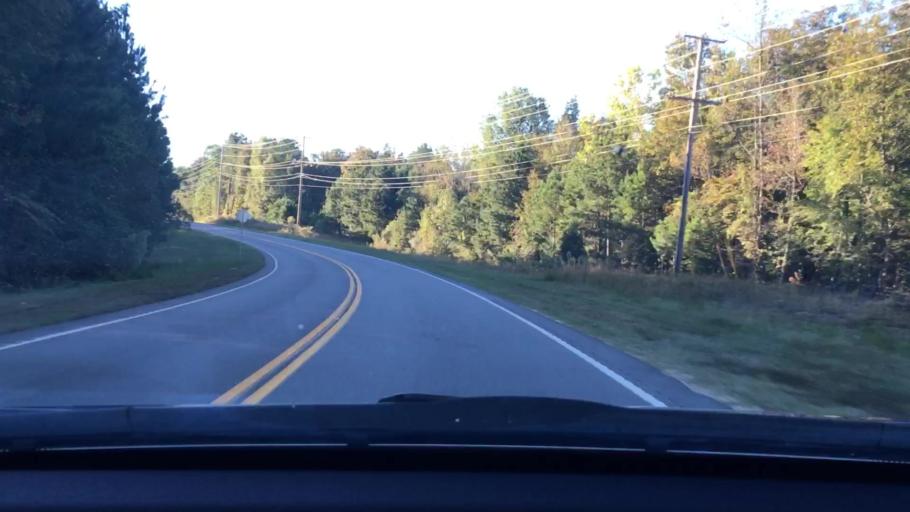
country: US
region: South Carolina
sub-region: Lexington County
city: Irmo
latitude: 34.1013
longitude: -81.1696
